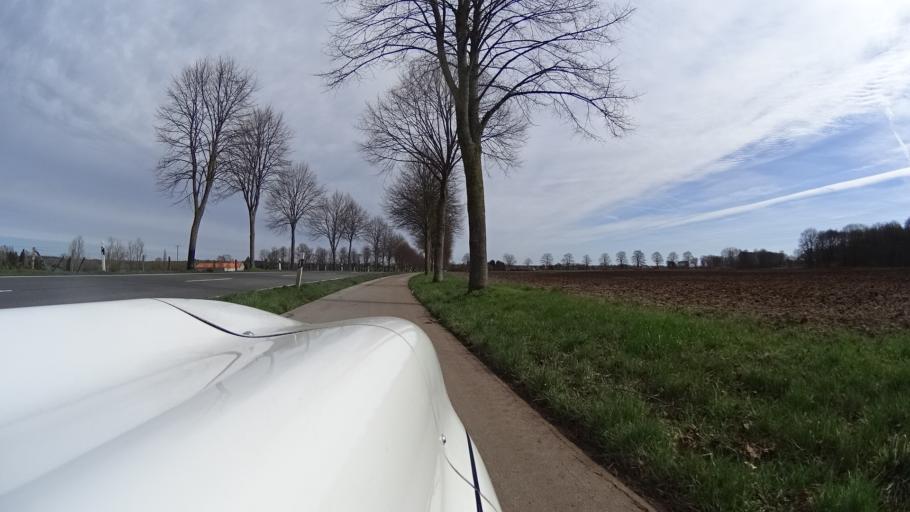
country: NL
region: Limburg
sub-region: Gemeente Gennep
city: Gennep
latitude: 51.7032
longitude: 6.0598
